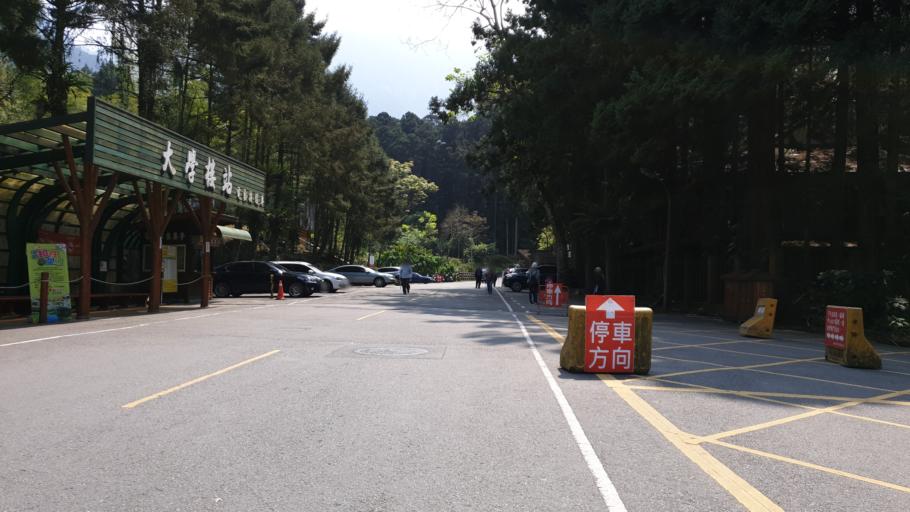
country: TW
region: Taiwan
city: Lugu
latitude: 23.6745
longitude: 120.7979
